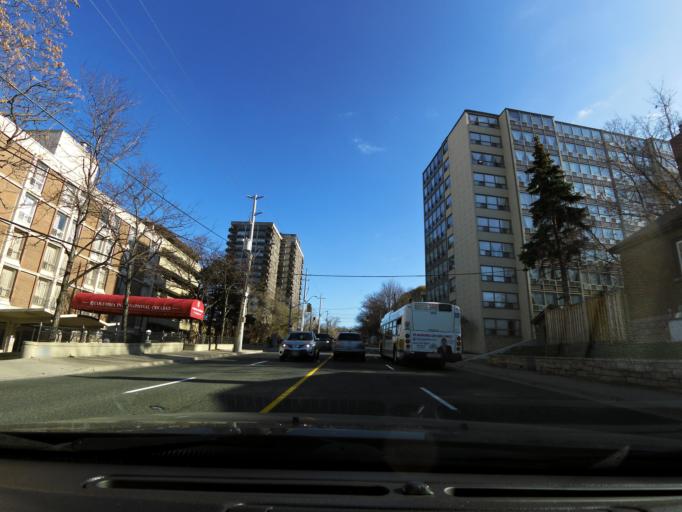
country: CA
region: Ontario
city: Hamilton
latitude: 43.2471
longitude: -79.8687
